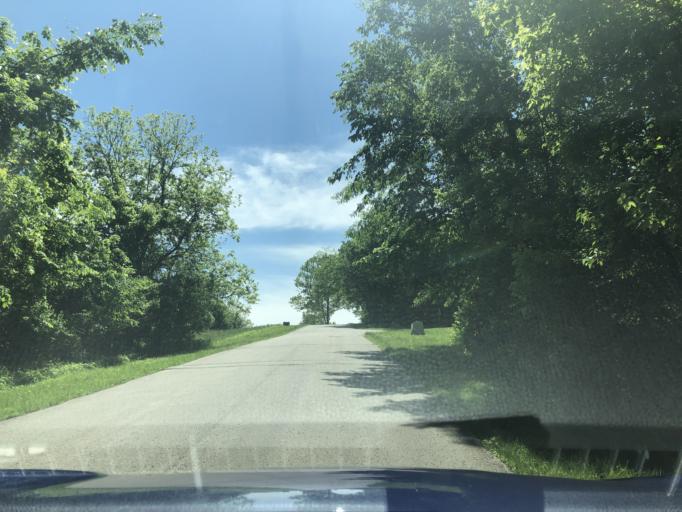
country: US
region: Missouri
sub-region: Platte County
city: Weston
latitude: 39.3931
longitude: -94.8690
